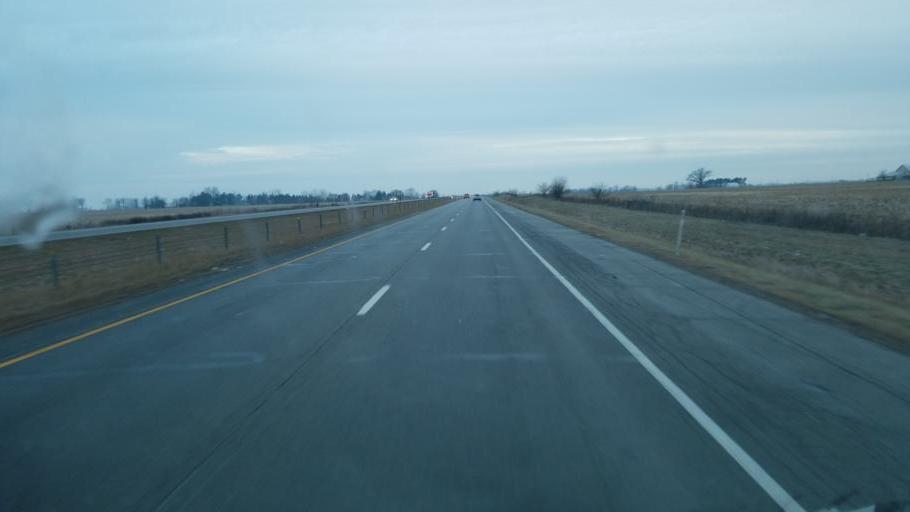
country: US
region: Indiana
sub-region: Henry County
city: Knightstown
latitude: 39.8261
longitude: -85.6260
